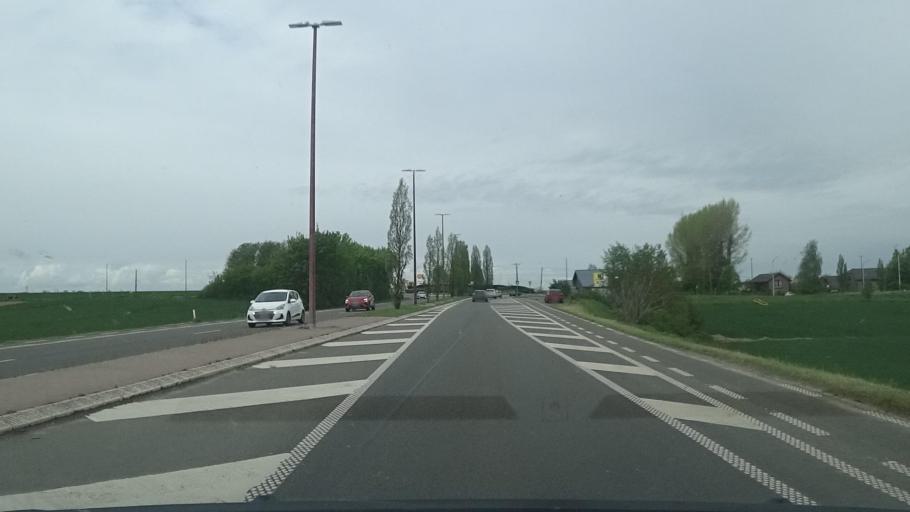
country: BE
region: Wallonia
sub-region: Province de Namur
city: Gembloux
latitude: 50.5168
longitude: 4.7682
